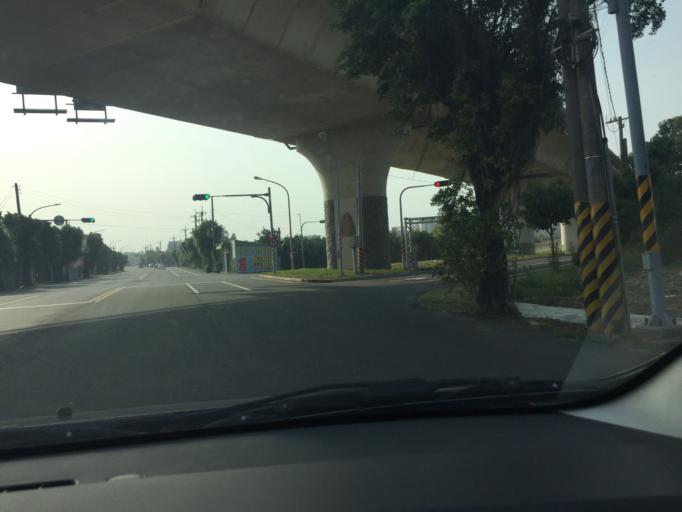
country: TW
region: Taiwan
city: Xinying
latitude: 23.1896
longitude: 120.2761
